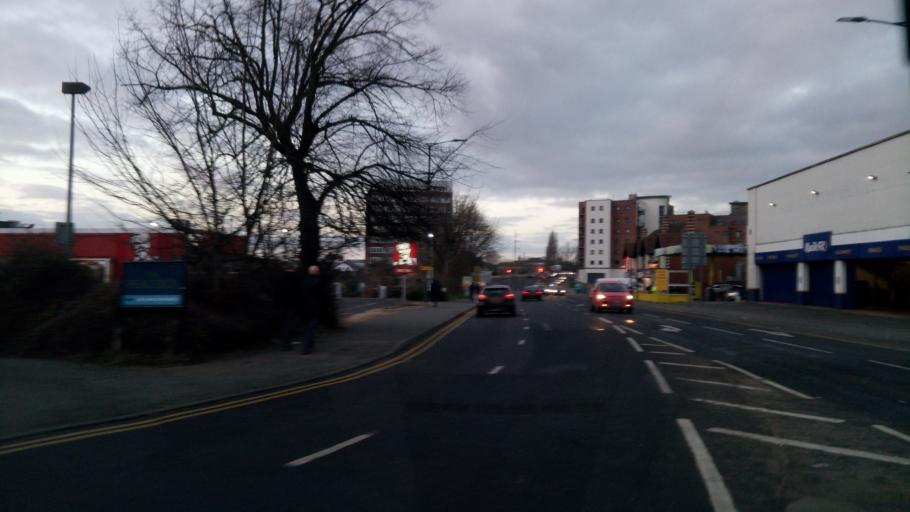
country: GB
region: England
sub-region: Peterborough
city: Peterborough
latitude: 52.5640
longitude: -0.2423
